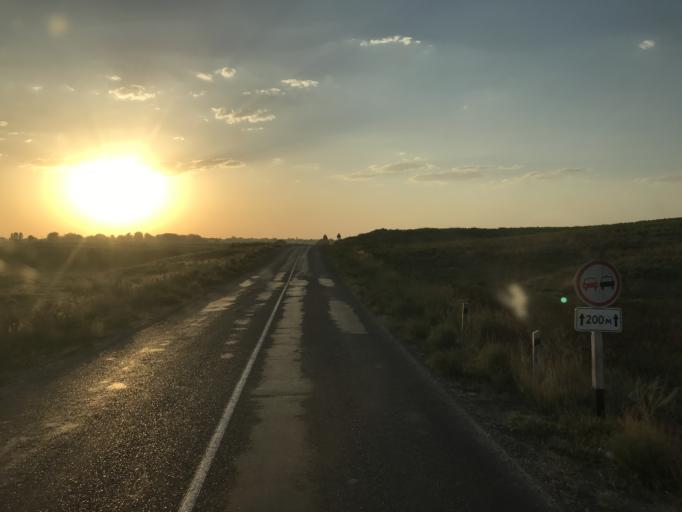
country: UZ
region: Toshkent
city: Yangiyul
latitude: 41.3505
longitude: 68.8673
